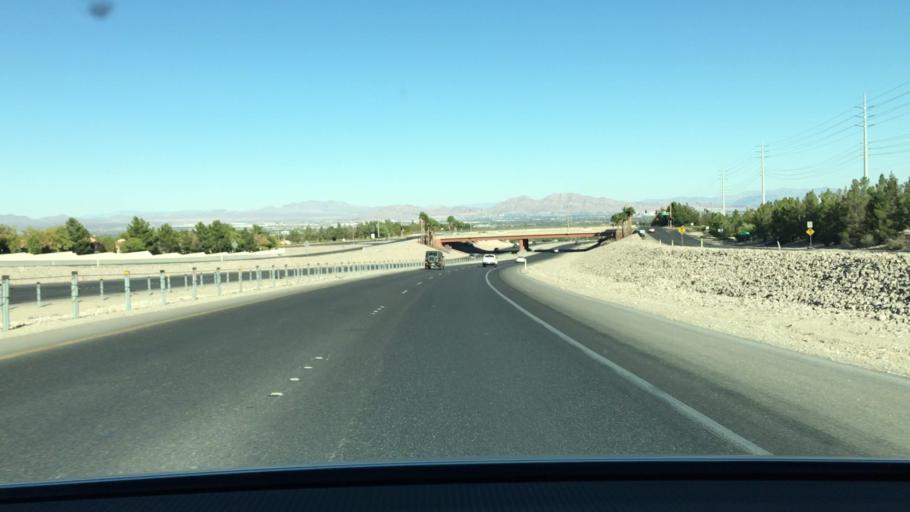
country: US
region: Nevada
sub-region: Clark County
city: Summerlin South
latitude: 36.1937
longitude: -115.3276
